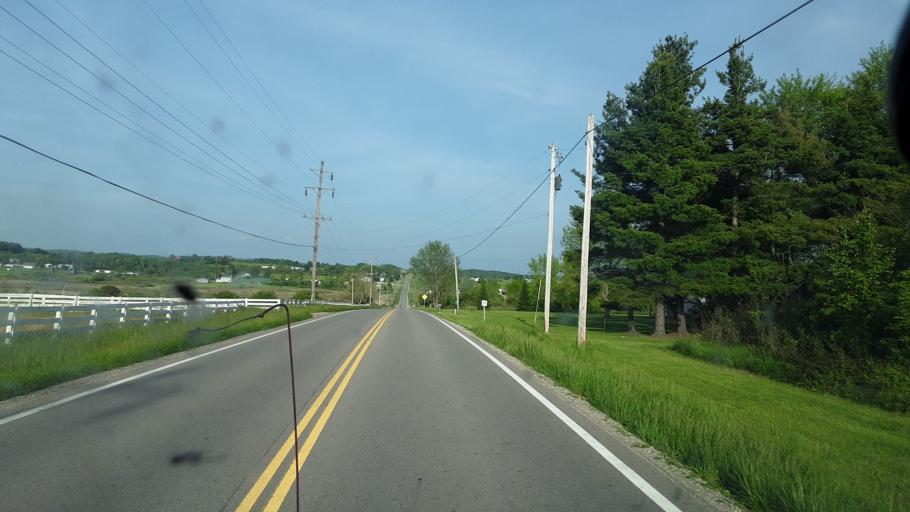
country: US
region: Ohio
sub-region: Ross County
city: Kingston
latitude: 39.5149
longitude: -82.8029
